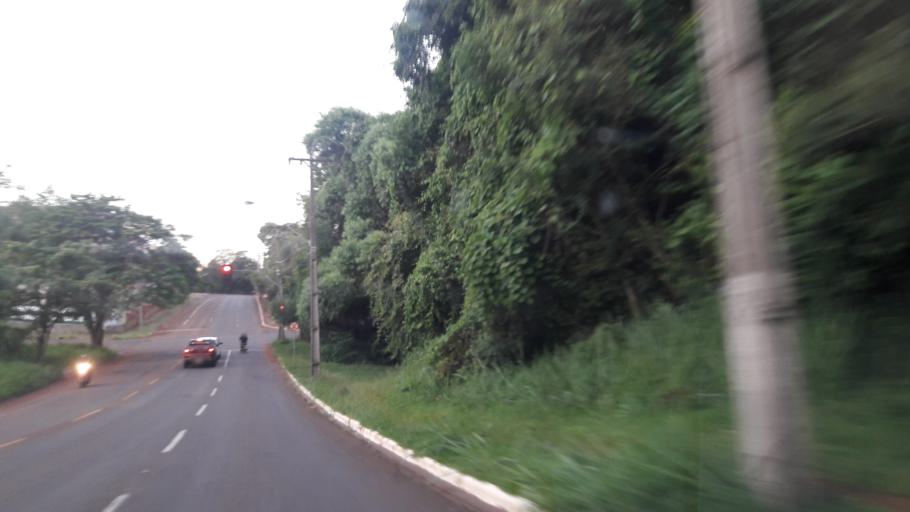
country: BR
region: Parana
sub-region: Cascavel
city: Cascavel
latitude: -24.9591
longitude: -53.4499
